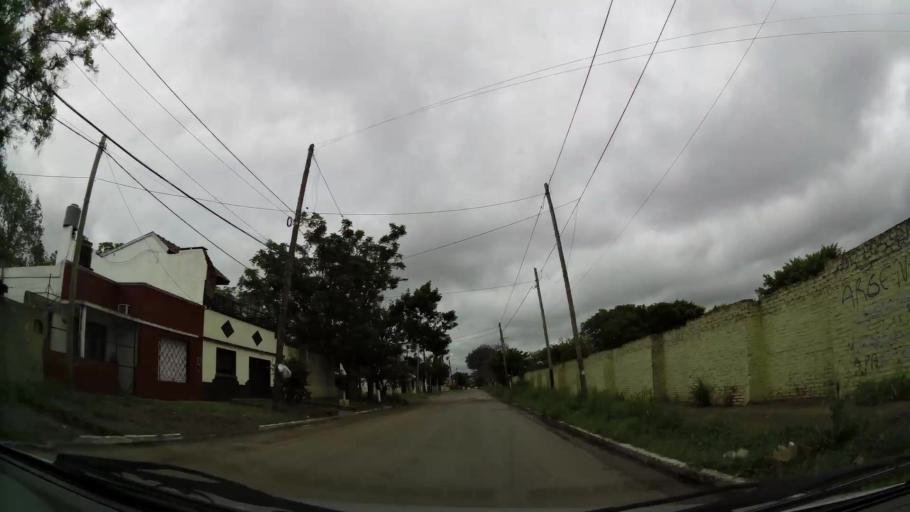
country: AR
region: Buenos Aires
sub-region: Partido de Lanus
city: Lanus
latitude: -34.7302
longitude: -58.3790
